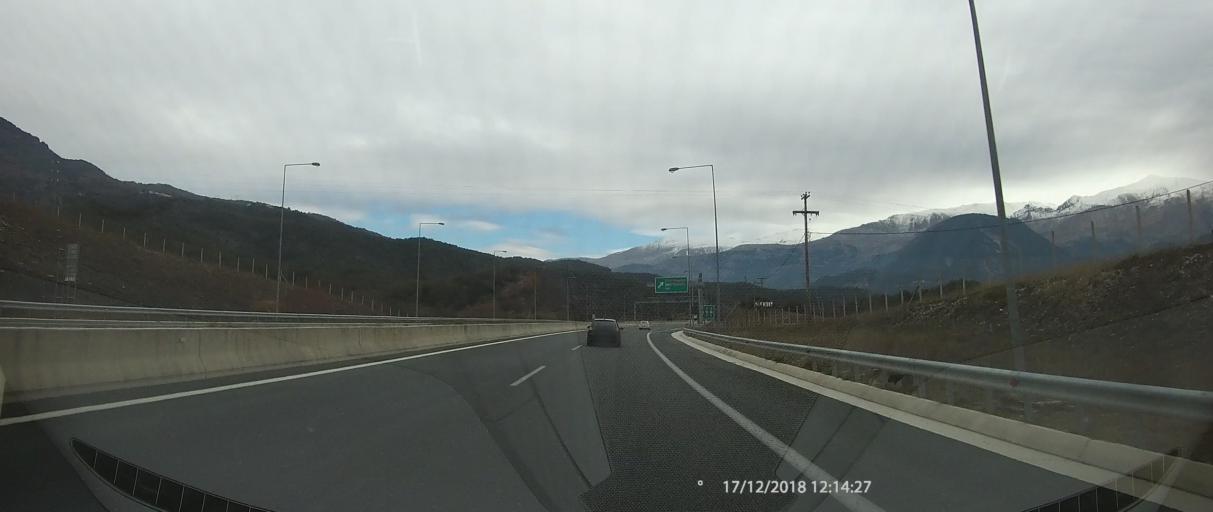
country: GR
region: Epirus
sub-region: Nomos Ioanninon
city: Katsikas
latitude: 39.7180
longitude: 20.9978
